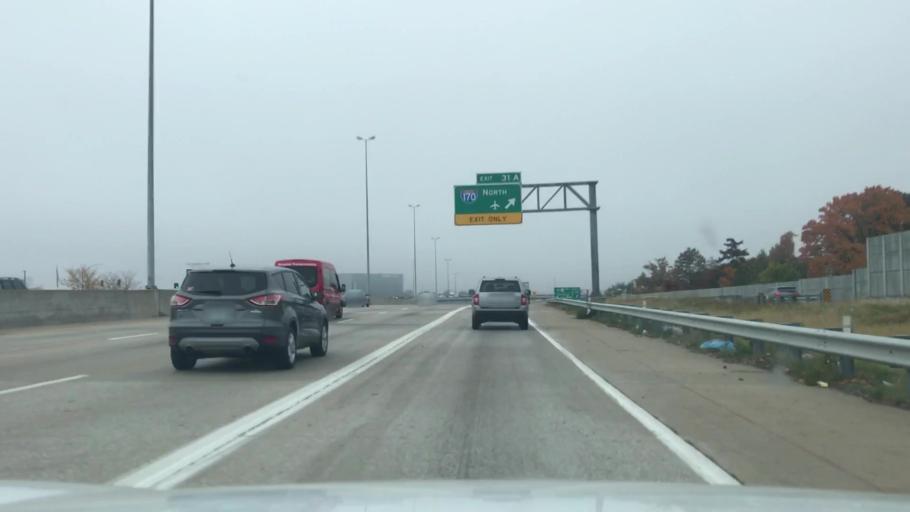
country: US
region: Missouri
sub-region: Saint Louis County
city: Brentwood
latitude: 38.6299
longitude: -90.3379
